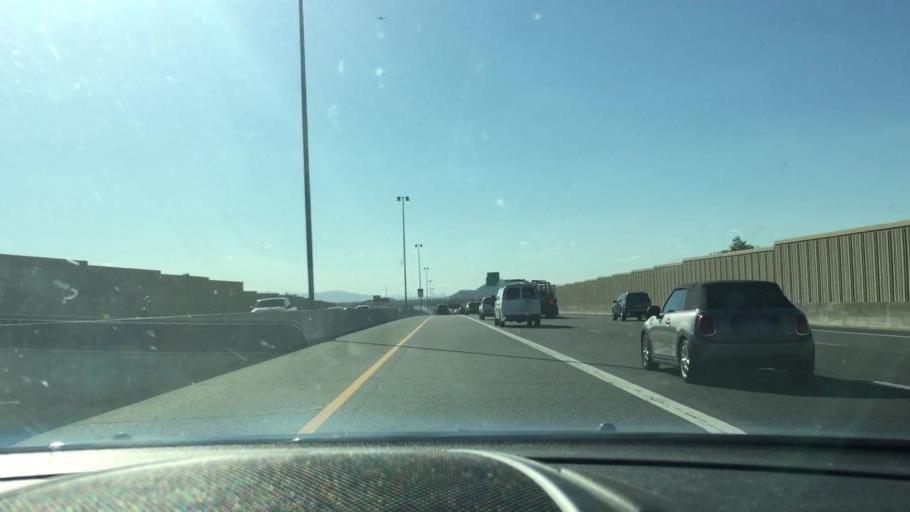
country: US
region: Arizona
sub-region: Maricopa County
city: Paradise Valley
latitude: 33.6709
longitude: -112.0475
